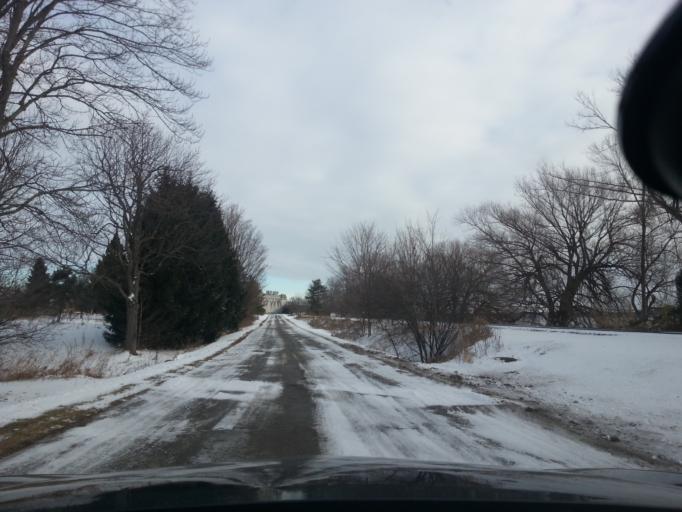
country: US
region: New York
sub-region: St. Lawrence County
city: Ogdensburg
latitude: 44.7249
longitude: -75.4805
